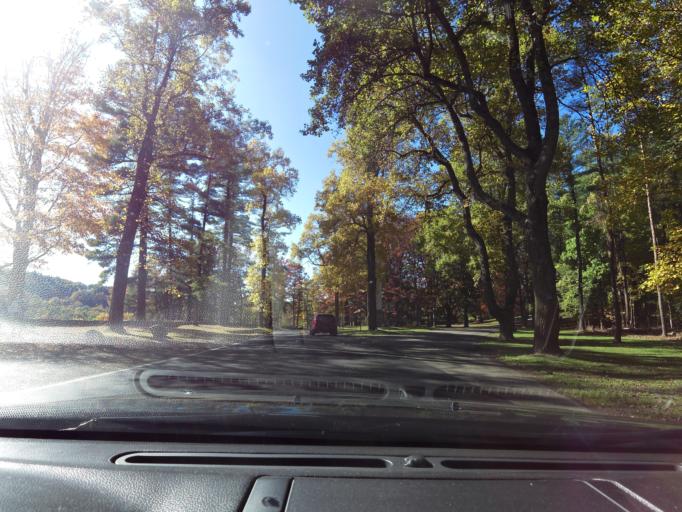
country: US
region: New York
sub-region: Wyoming County
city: Castile
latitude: 42.5882
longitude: -78.0375
